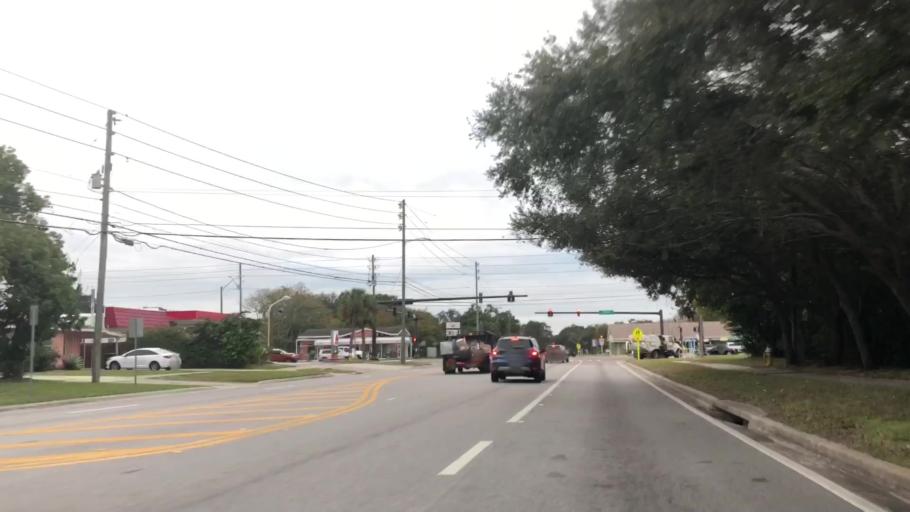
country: US
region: Florida
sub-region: Pinellas County
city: Clearwater
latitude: 27.9689
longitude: -82.7547
